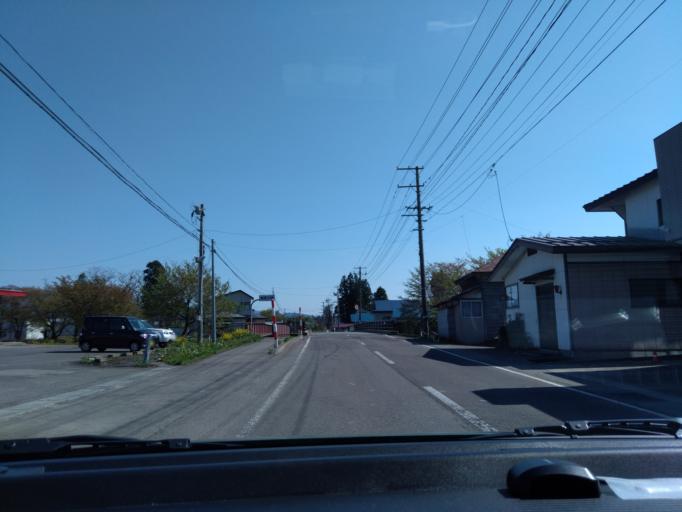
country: JP
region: Akita
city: Kakunodatemachi
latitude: 39.4955
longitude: 140.5940
